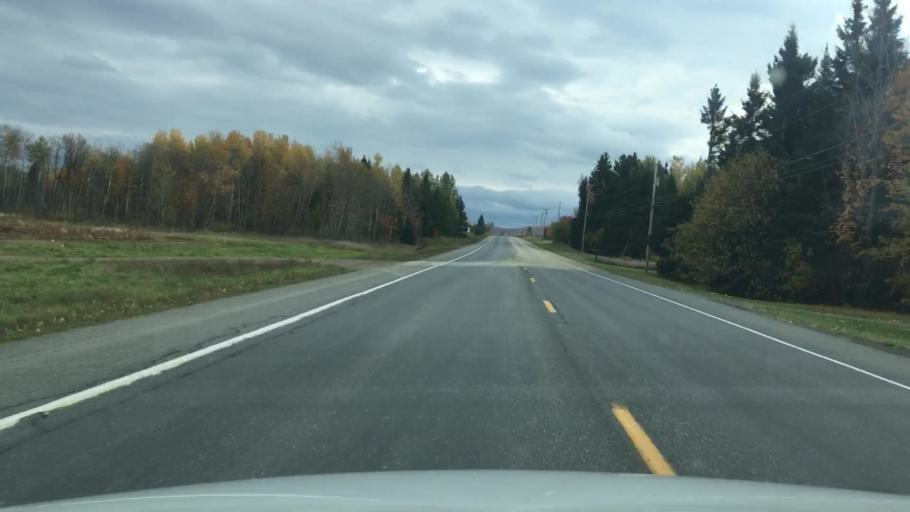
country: US
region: Maine
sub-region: Aroostook County
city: Easton
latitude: 46.5613
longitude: -67.9444
